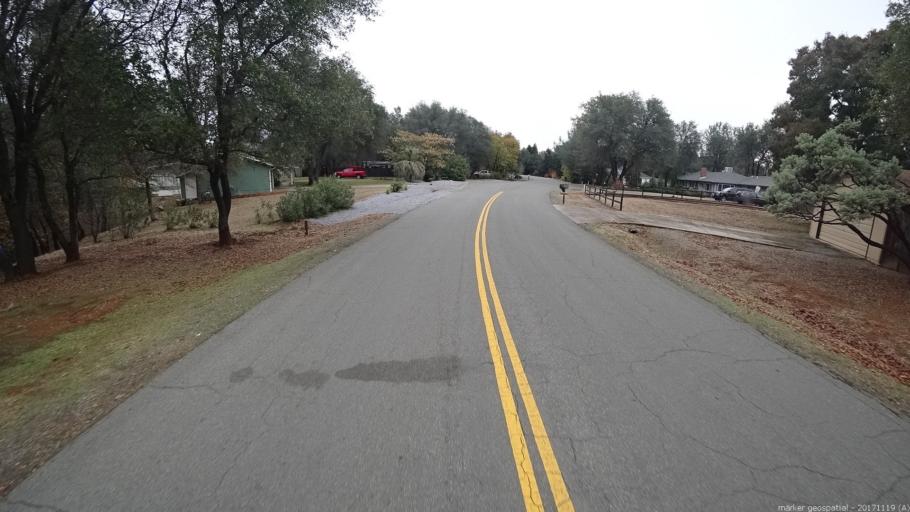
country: US
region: California
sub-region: Shasta County
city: Redding
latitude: 40.4950
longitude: -122.4120
